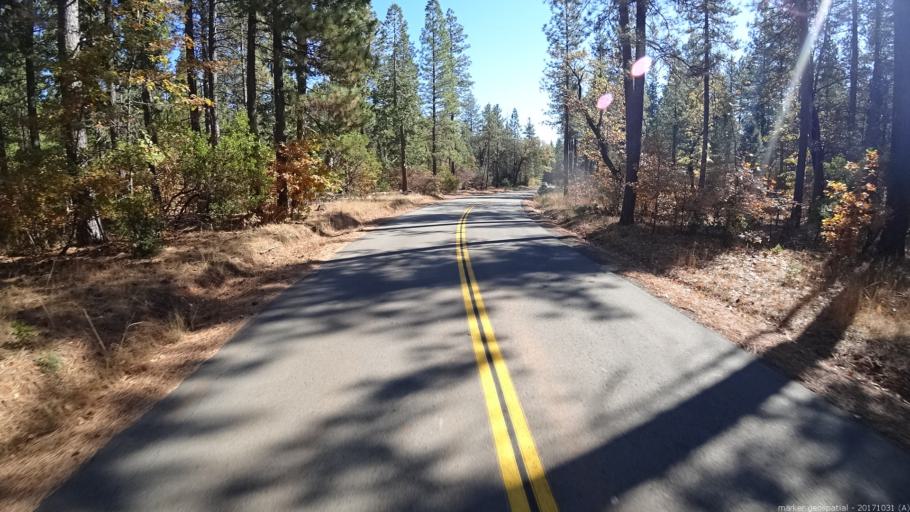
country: US
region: California
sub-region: Shasta County
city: Shingletown
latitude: 40.4845
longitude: -121.8787
